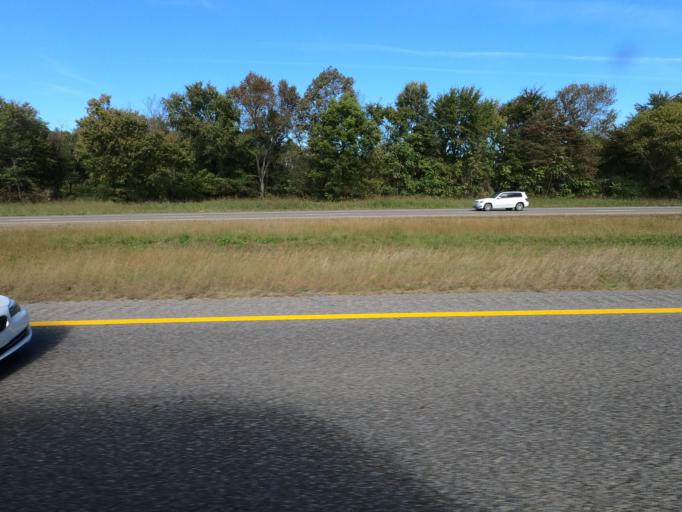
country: US
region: Tennessee
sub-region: Crockett County
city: Bells
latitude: 35.5777
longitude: -89.1185
